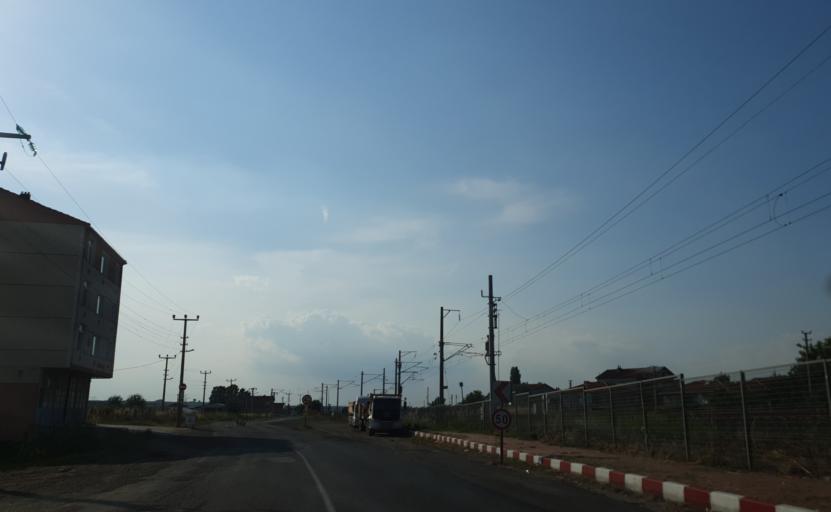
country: TR
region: Tekirdag
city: Muratli
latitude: 41.1769
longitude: 27.4906
